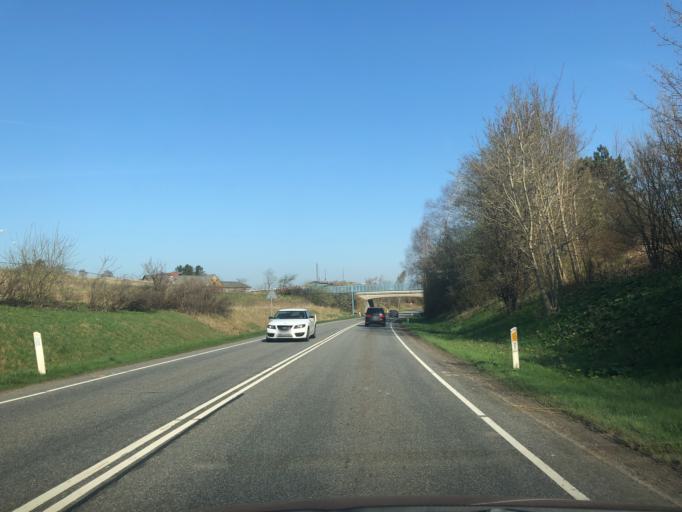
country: DK
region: Zealand
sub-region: Faxe Kommune
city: Haslev
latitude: 55.3213
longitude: 11.9445
